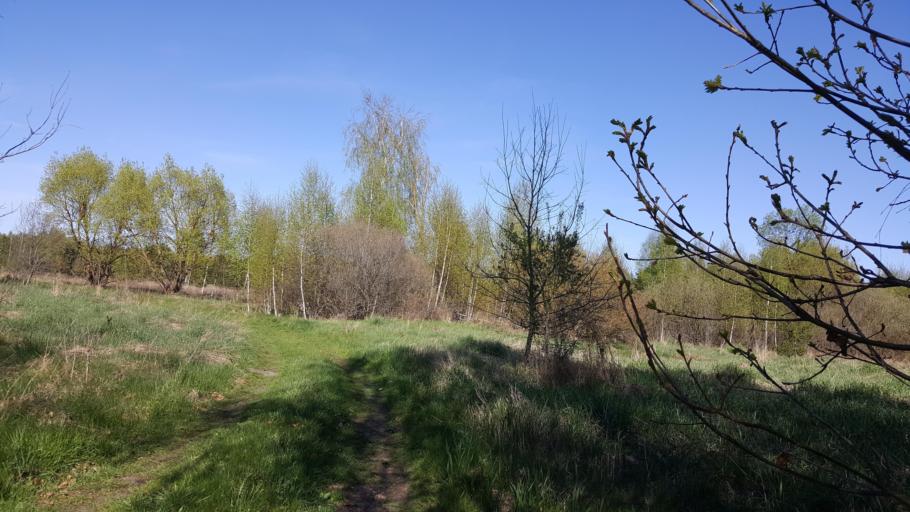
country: BY
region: Brest
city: Kamyanyets
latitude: 52.4357
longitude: 23.8742
